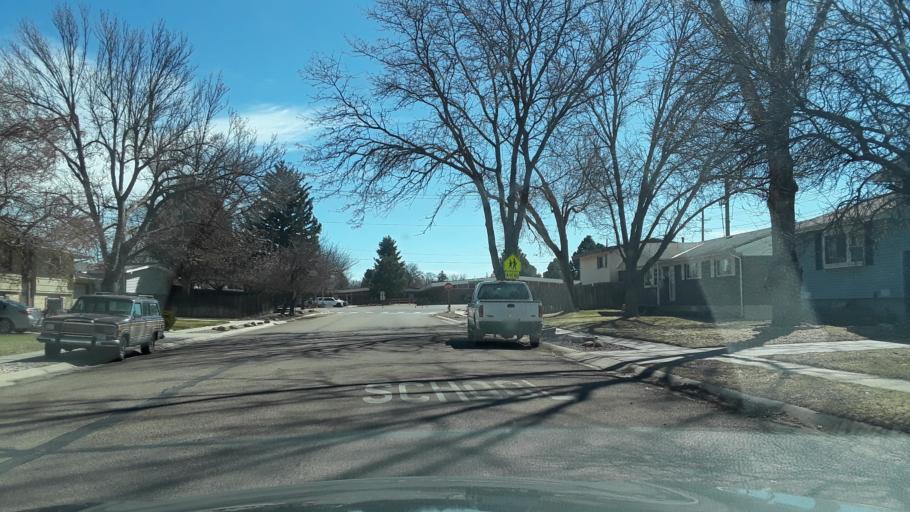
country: US
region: Colorado
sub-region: El Paso County
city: Colorado Springs
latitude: 38.8680
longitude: -104.8072
